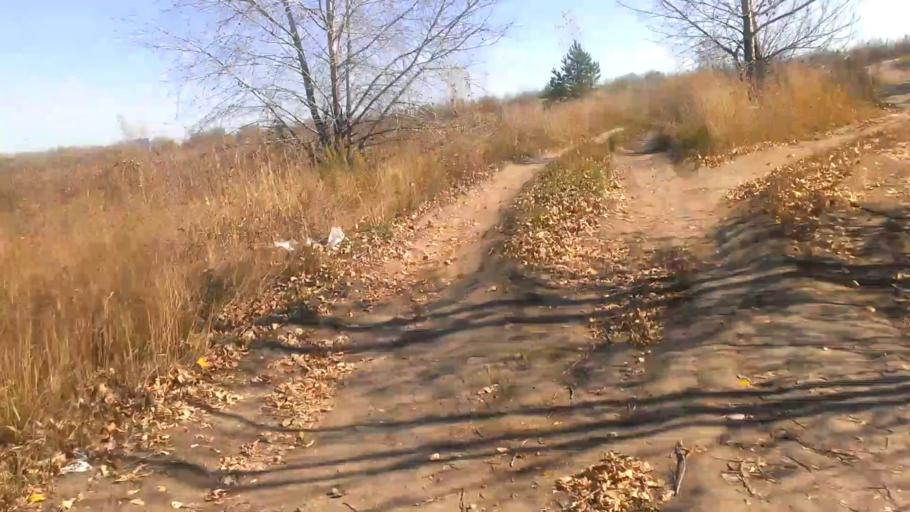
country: RU
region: Altai Krai
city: Novoaltaysk
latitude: 53.3717
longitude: 83.9505
